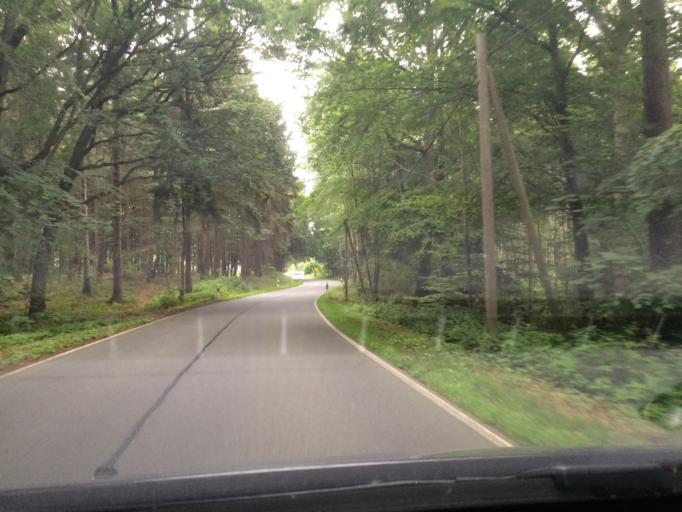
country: DE
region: Mecklenburg-Vorpommern
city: Prohn
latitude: 54.4291
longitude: 13.0264
